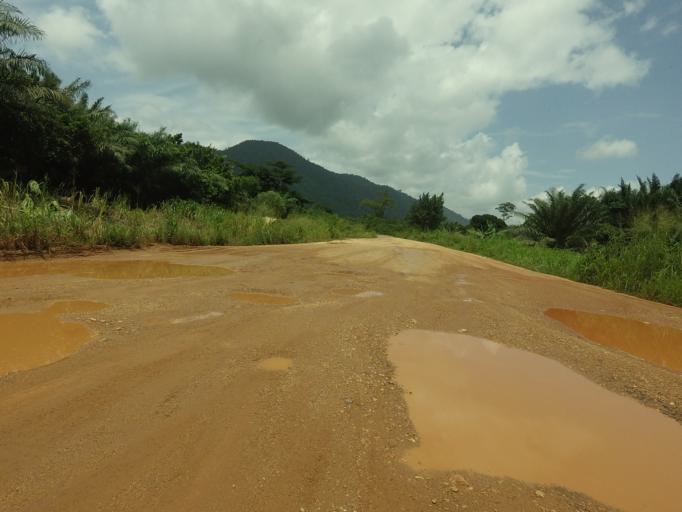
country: GH
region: Volta
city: Ho
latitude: 6.7724
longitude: 0.3643
